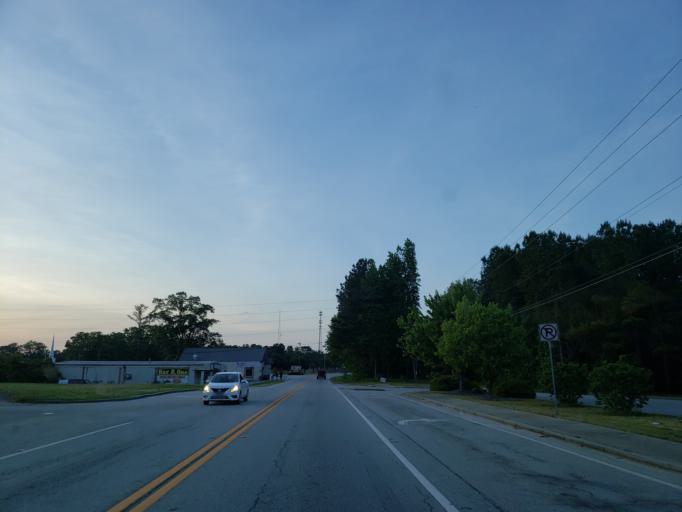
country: US
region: Georgia
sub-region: Douglas County
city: Douglasville
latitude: 33.6686
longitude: -84.8056
